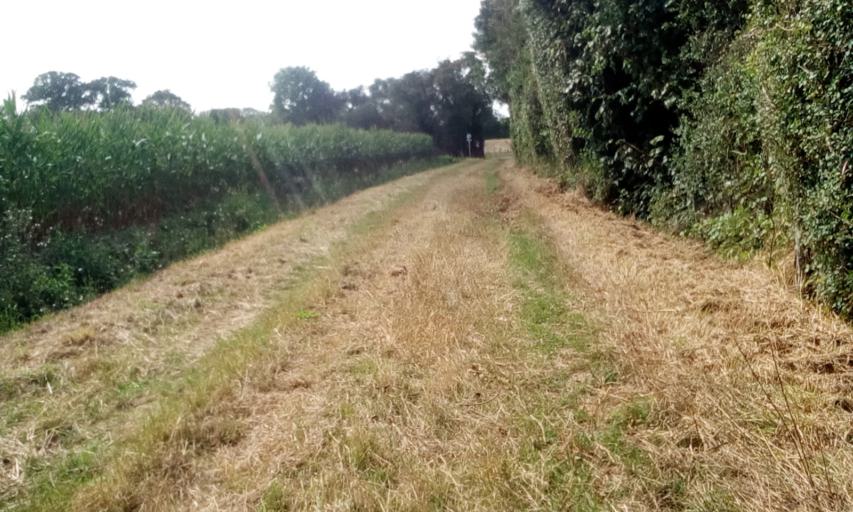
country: FR
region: Lower Normandy
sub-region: Departement du Calvados
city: Argences
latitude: 49.1460
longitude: -0.1242
